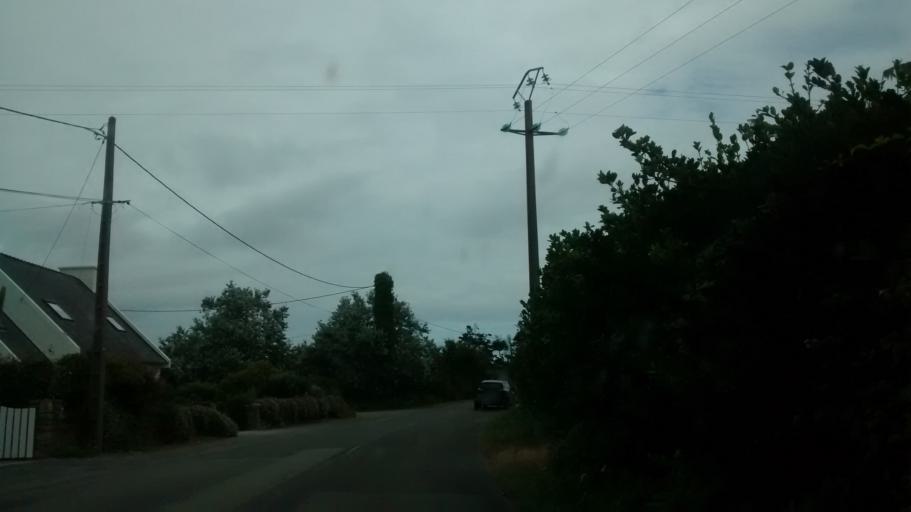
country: FR
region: Brittany
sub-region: Departement du Finistere
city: Guisseny
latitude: 48.6367
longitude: -4.4274
